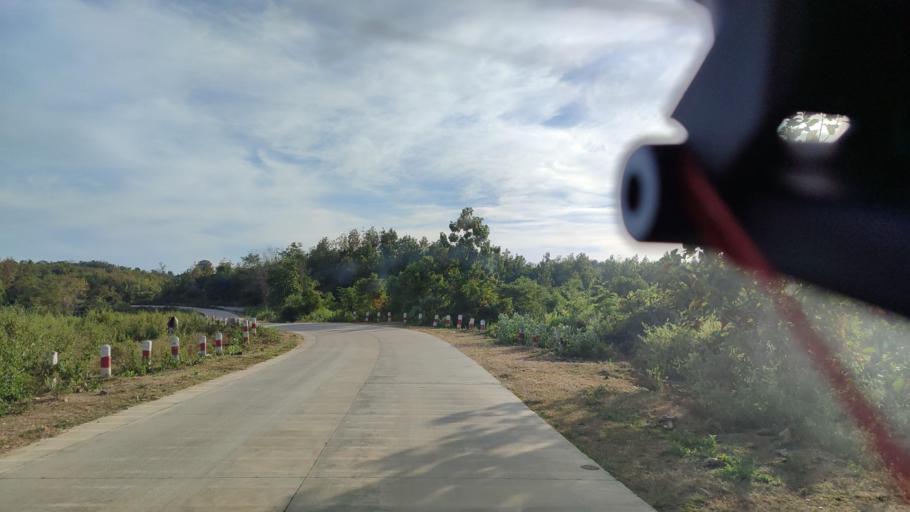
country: MM
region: Magway
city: Taungdwingyi
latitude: 20.0290
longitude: 95.7888
